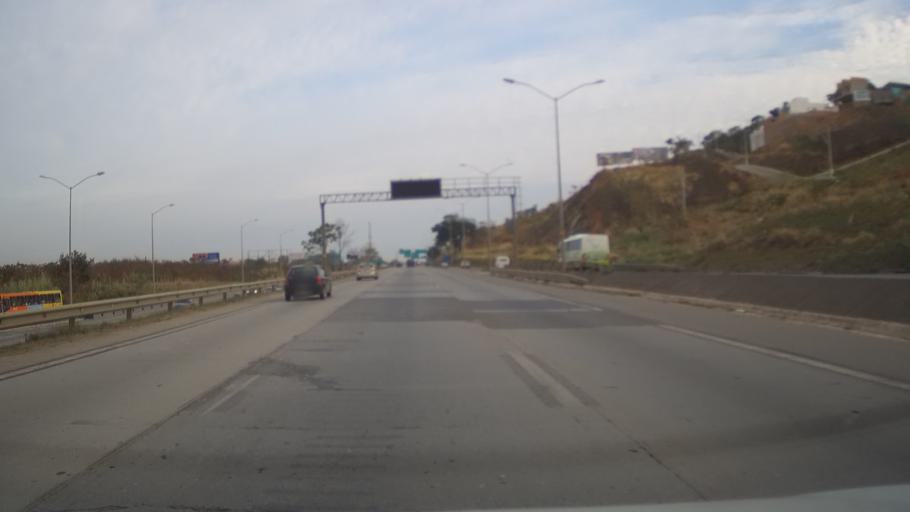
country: BR
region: Minas Gerais
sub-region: Vespasiano
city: Vespasiano
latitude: -19.7691
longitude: -43.9483
